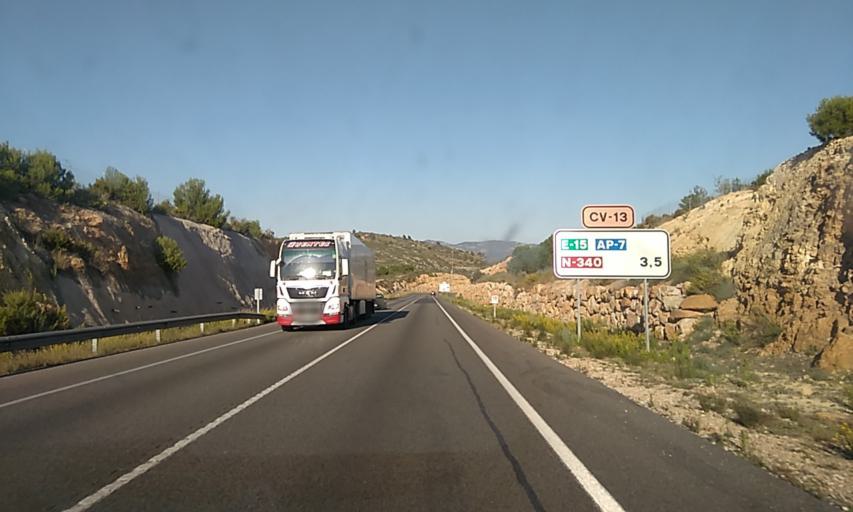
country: ES
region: Valencia
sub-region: Provincia de Castello
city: Torreblanca
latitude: 40.2240
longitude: 0.1762
